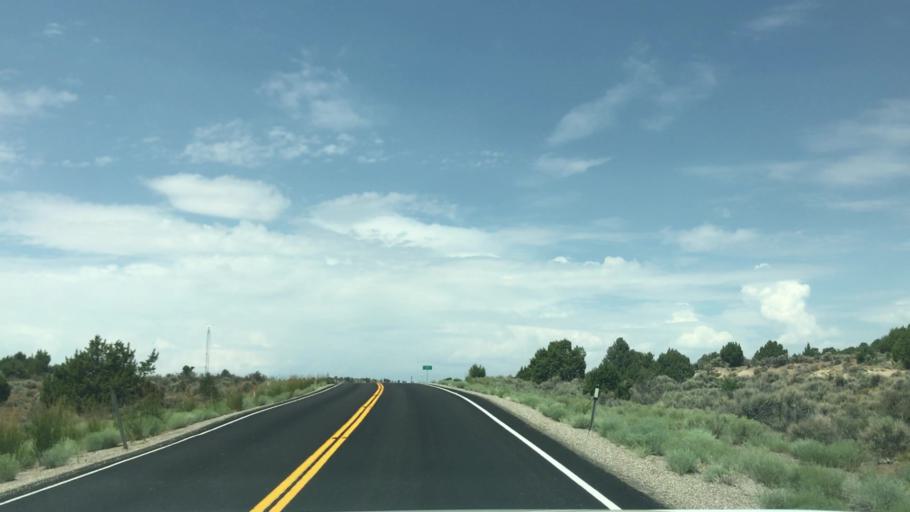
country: US
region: Nevada
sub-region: Eureka County
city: Eureka
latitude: 39.3970
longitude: -115.4661
